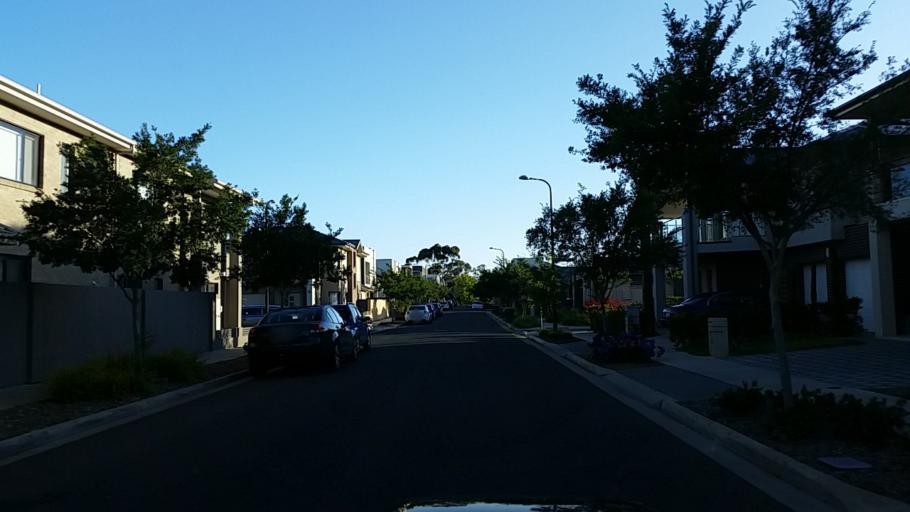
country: AU
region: South Australia
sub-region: Charles Sturt
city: Woodville North
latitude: -34.8710
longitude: 138.5335
